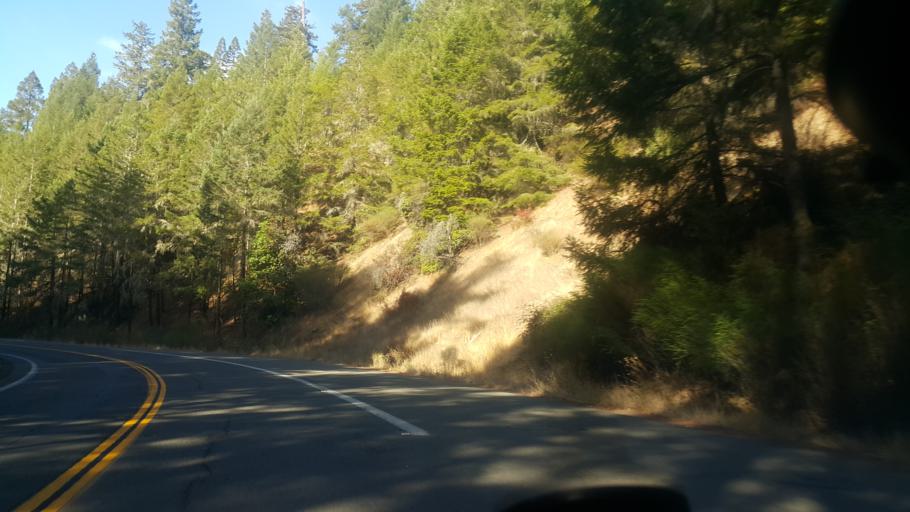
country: US
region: California
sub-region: Mendocino County
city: Brooktrails
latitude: 39.3477
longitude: -123.5199
